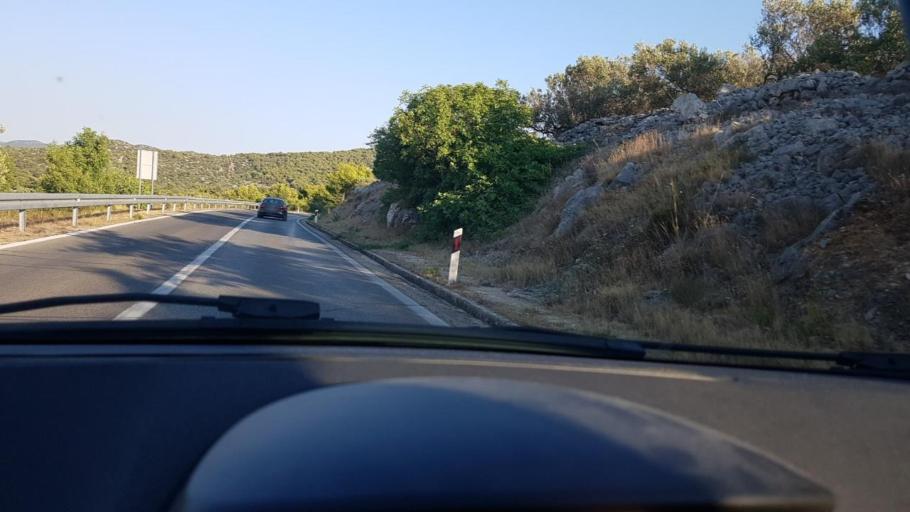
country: HR
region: Sibensko-Kniniska
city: Murter
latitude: 43.8093
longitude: 15.6036
